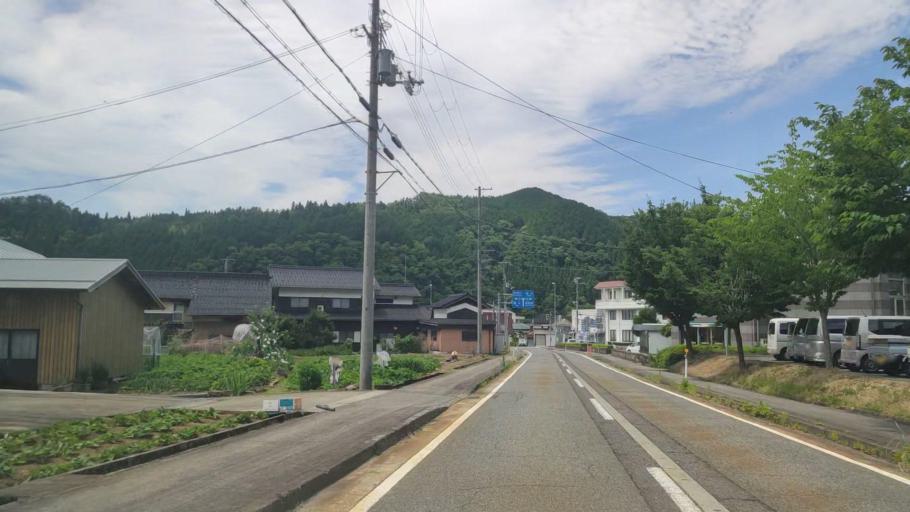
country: JP
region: Hyogo
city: Toyooka
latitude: 35.4738
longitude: 134.5960
